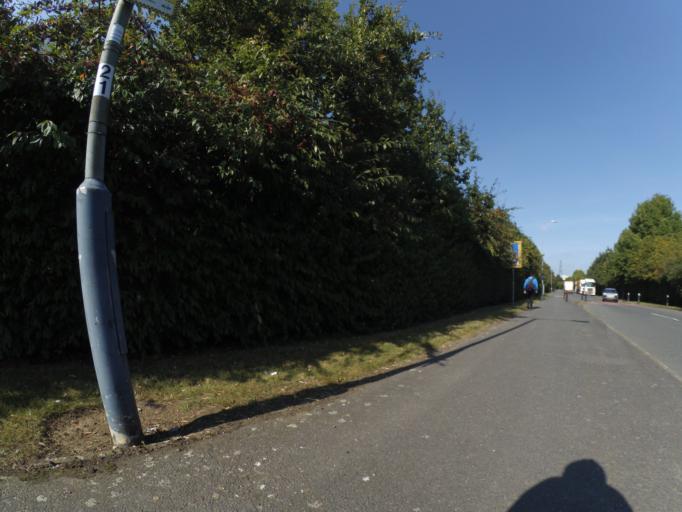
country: GB
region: England
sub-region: Warwickshire
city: Rugby
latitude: 52.3989
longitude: -1.2641
